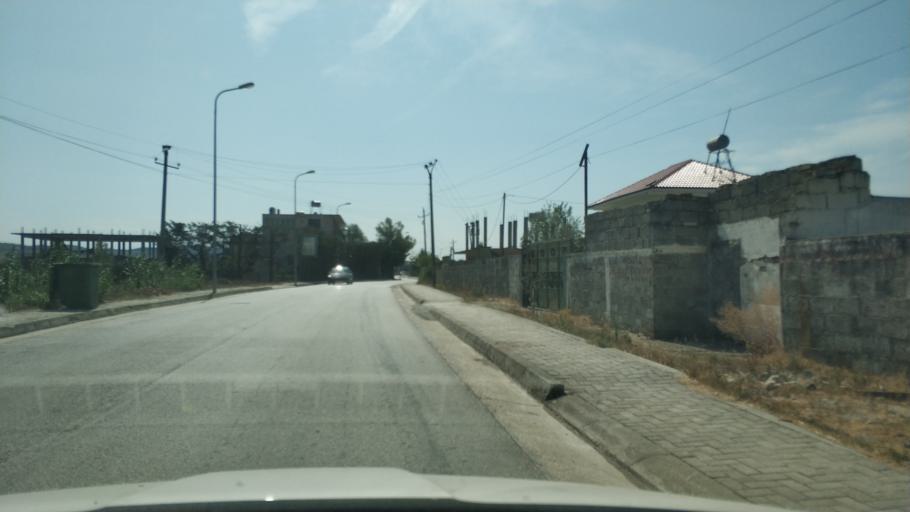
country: AL
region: Fier
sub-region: Rrethi i Lushnjes
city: Divjake
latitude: 40.9889
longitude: 19.5343
